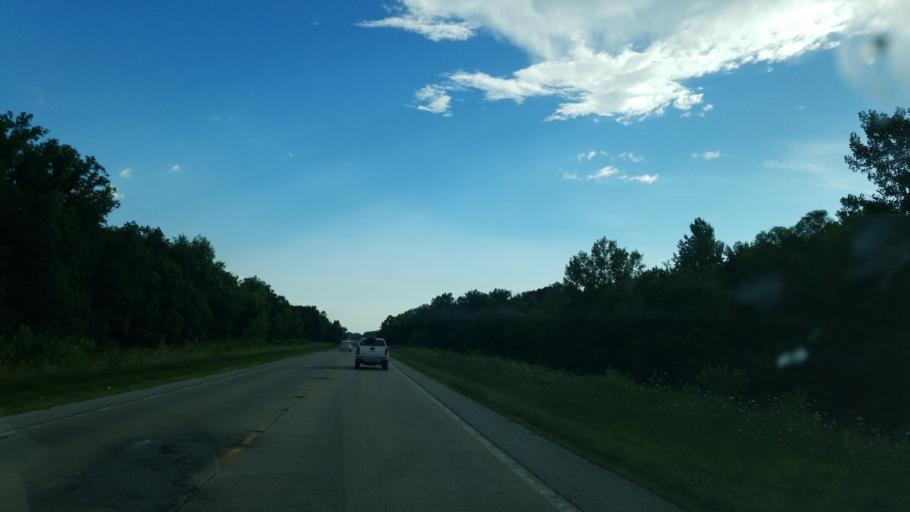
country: US
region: Illinois
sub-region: Marion County
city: Central City
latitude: 38.5660
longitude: -89.1159
